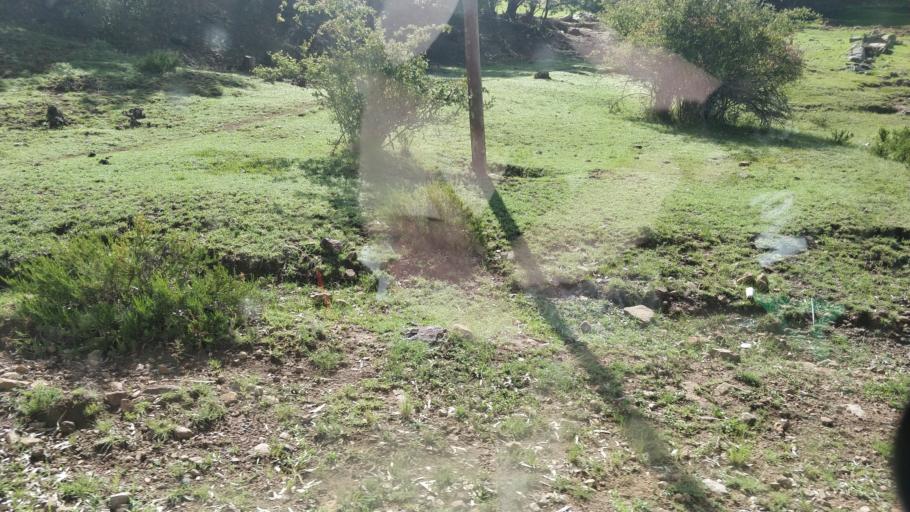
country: LS
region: Maseru
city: Nako
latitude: -29.6266
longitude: 27.5127
